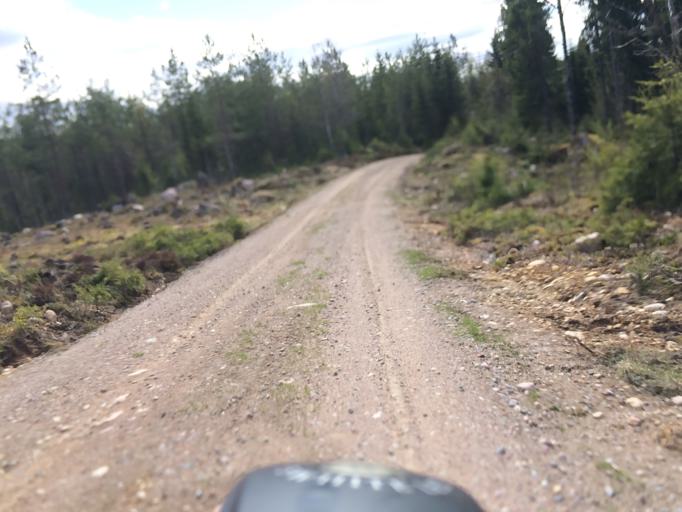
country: SE
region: OErebro
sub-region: Hallefors Kommun
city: Haellefors
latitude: 60.0492
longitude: 14.5162
